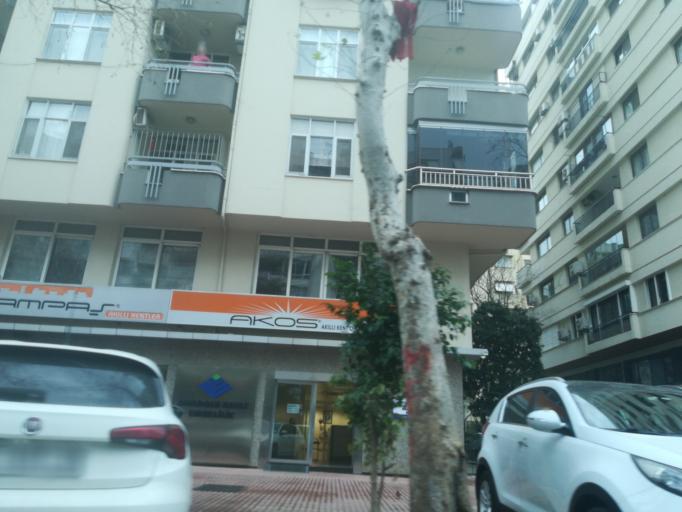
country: TR
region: Adana
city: Adana
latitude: 36.9978
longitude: 35.3212
